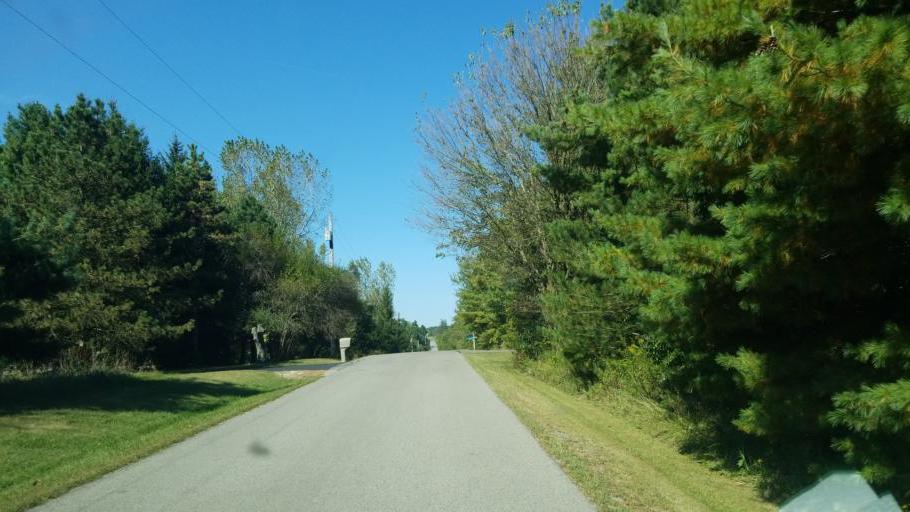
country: US
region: Ohio
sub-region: Logan County
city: Bellefontaine
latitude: 40.3092
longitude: -83.7162
